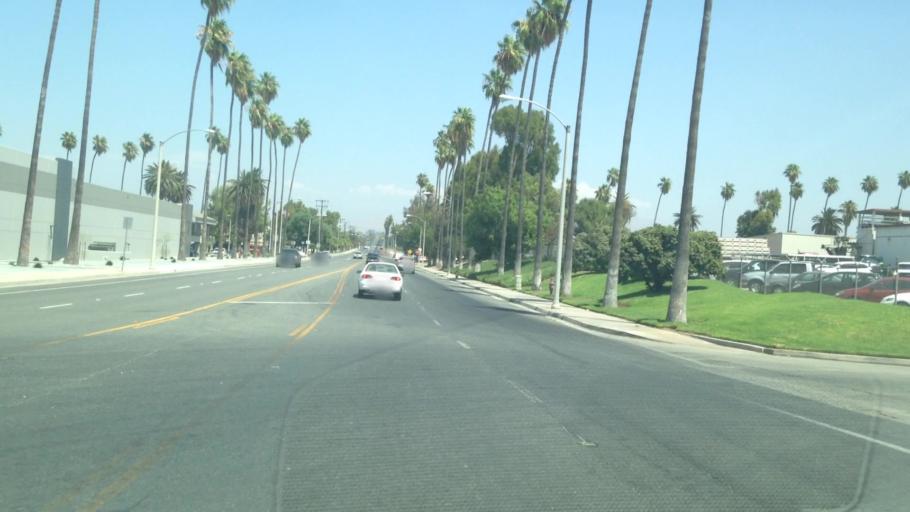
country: US
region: California
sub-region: Riverside County
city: Riverside
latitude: 33.9237
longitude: -117.4085
